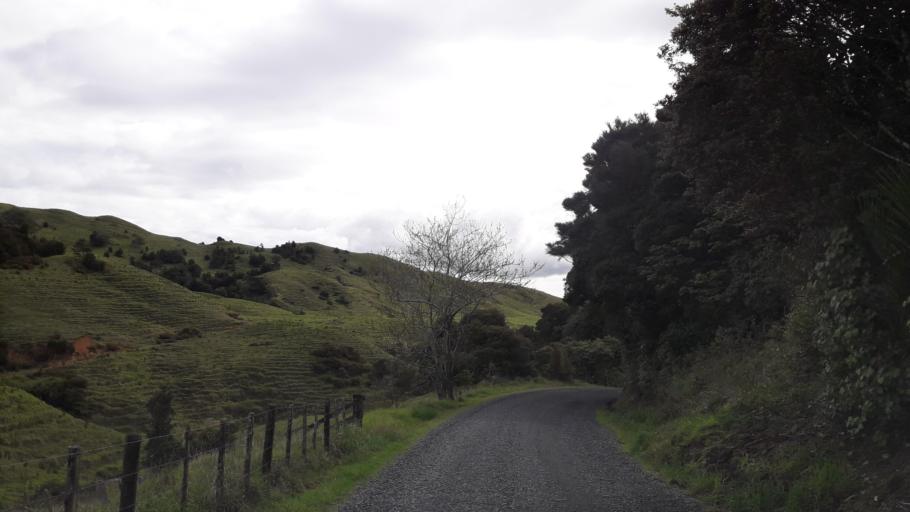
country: NZ
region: Northland
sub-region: Far North District
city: Taipa
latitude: -35.0987
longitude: 173.5438
